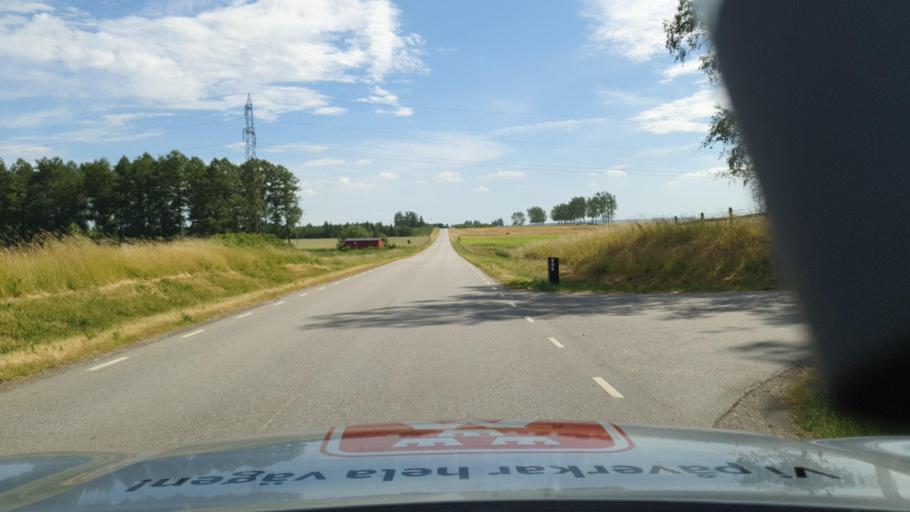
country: SE
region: Skane
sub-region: Sjobo Kommun
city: Sjoebo
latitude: 55.6292
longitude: 13.6567
